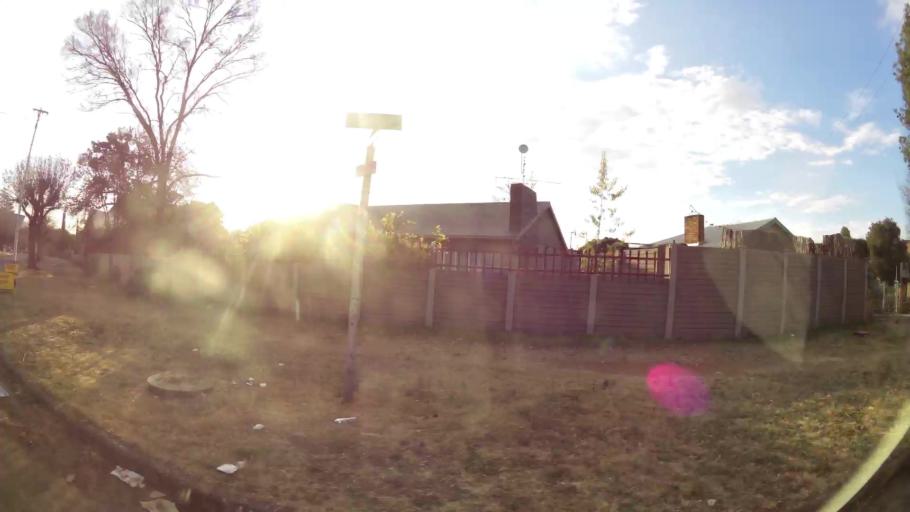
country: ZA
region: Orange Free State
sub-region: Mangaung Metropolitan Municipality
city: Bloemfontein
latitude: -29.1420
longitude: 26.1953
